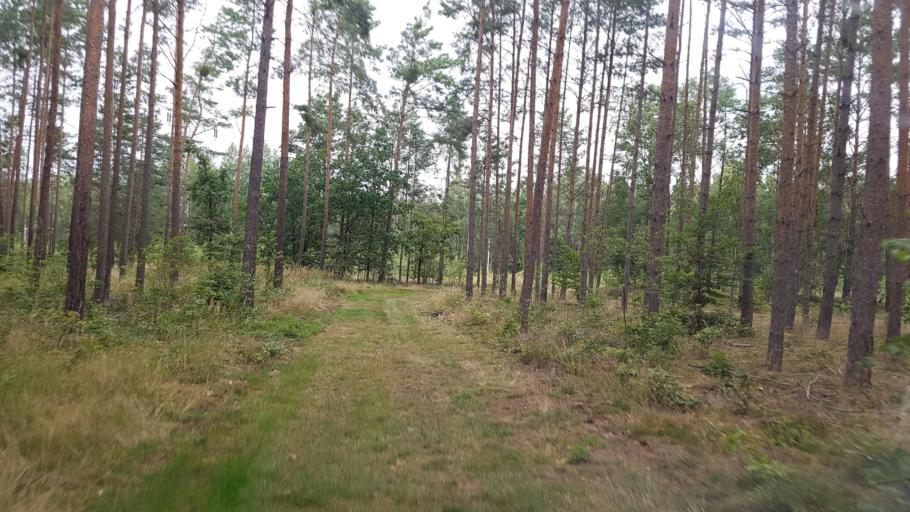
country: DE
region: Brandenburg
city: Schonborn
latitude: 51.6078
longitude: 13.5138
